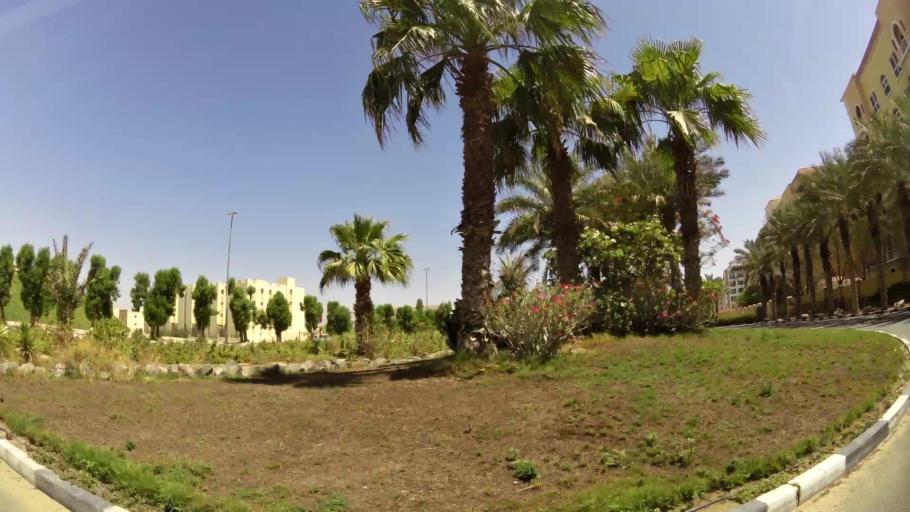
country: AE
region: Dubai
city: Dubai
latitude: 24.9874
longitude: 55.2006
